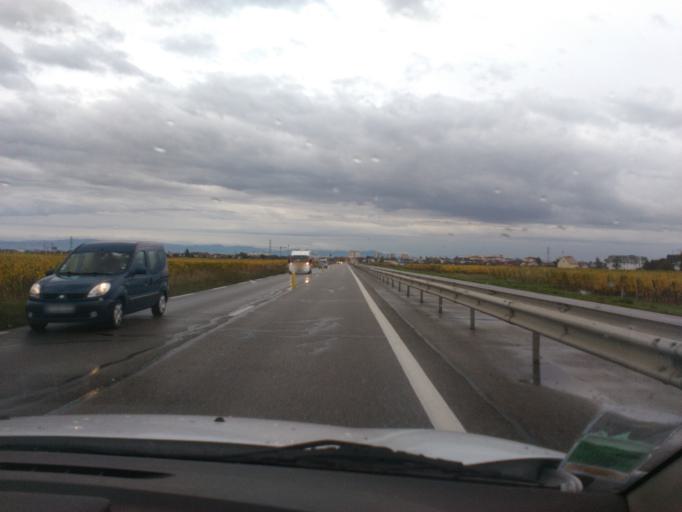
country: FR
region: Alsace
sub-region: Departement du Haut-Rhin
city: Ingersheim
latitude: 48.0965
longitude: 7.3139
